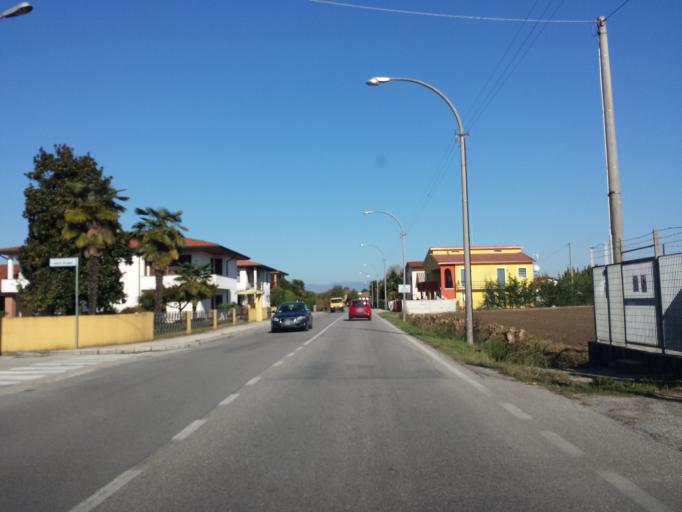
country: IT
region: Veneto
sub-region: Provincia di Vicenza
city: Camisano Vicentino
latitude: 45.5285
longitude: 11.7160
